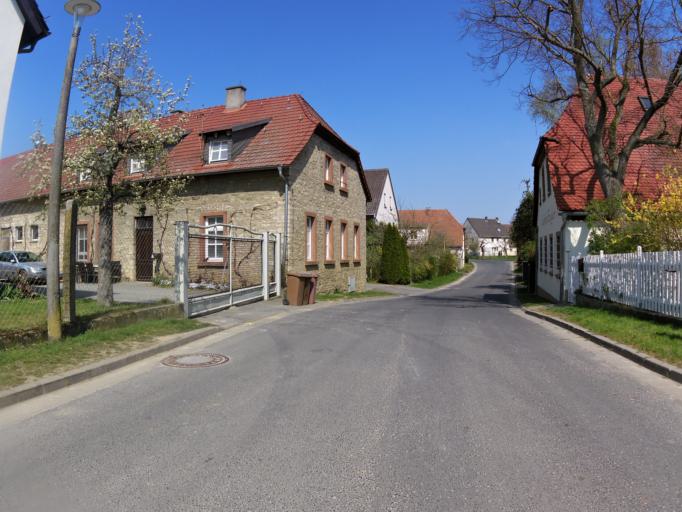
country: DE
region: Bavaria
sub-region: Regierungsbezirk Unterfranken
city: Rottendorf
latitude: 49.8114
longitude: 10.0554
